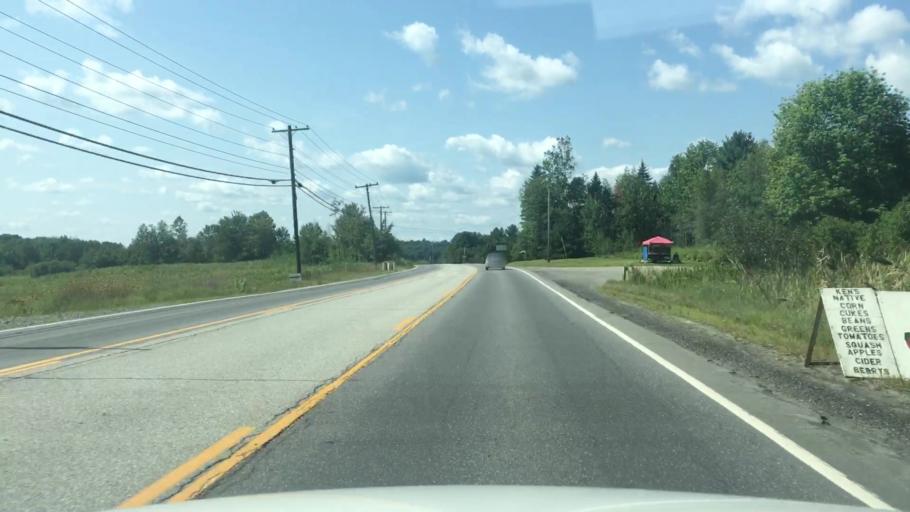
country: US
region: Maine
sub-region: Kennebec County
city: Manchester
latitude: 44.3233
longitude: -69.8476
